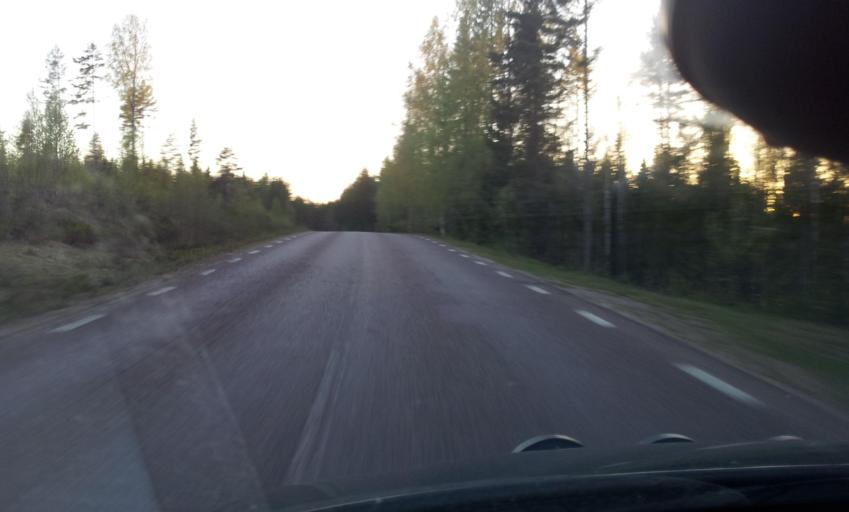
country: SE
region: Gaevleborg
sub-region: Bollnas Kommun
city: Bollnas
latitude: 61.3918
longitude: 16.4591
